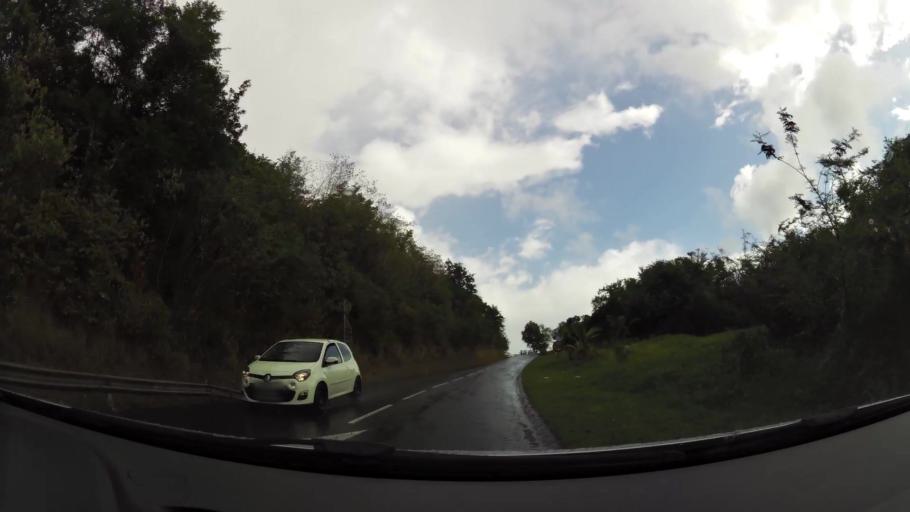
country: MQ
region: Martinique
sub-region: Martinique
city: Les Trois-Ilets
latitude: 14.5421
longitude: -61.0479
